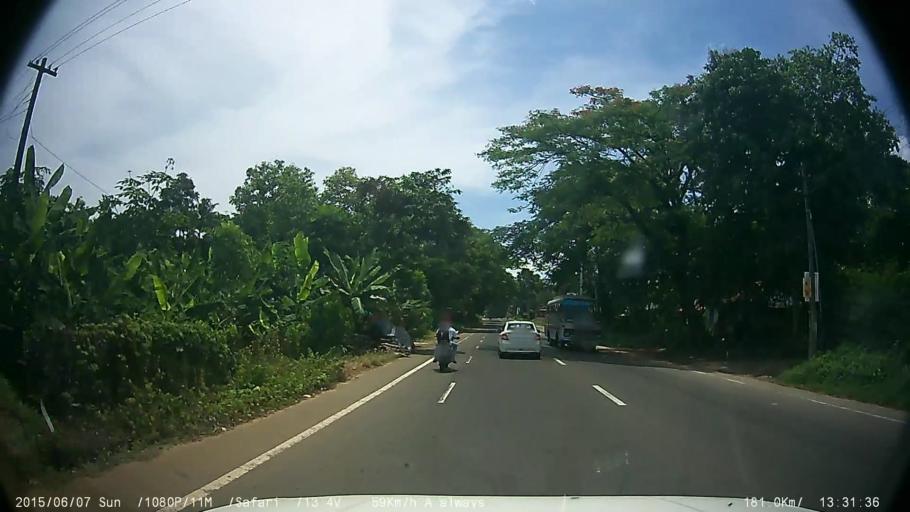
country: IN
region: Kerala
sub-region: Ernakulam
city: Muvattupula
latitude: 10.0423
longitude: 76.5370
